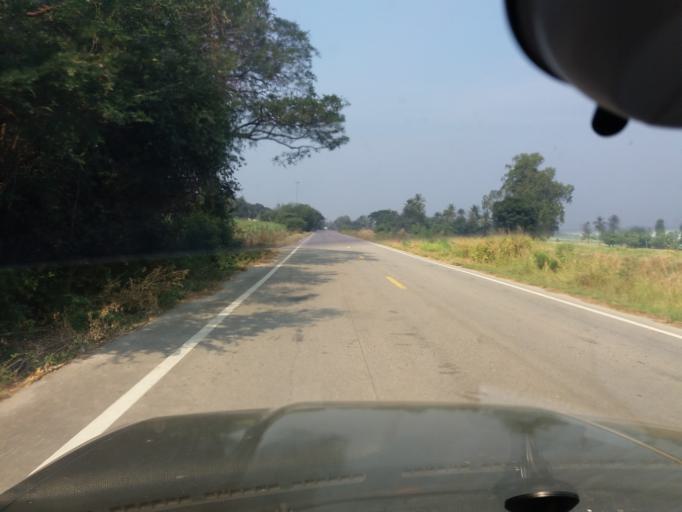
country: TH
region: Sing Buri
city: Bang Racham
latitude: 14.9068
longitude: 100.2618
